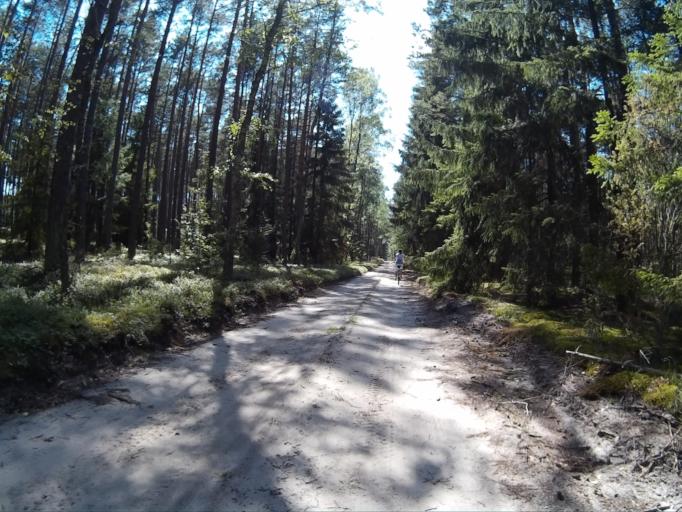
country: PL
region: Pomeranian Voivodeship
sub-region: Powiat chojnicki
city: Czersk
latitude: 53.7234
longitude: 17.8960
